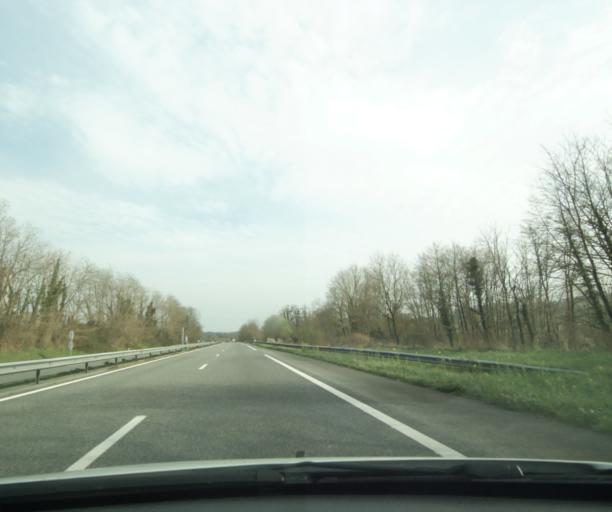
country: FR
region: Aquitaine
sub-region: Departement des Pyrenees-Atlantiques
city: Puyoo
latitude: 43.5083
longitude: -0.8780
